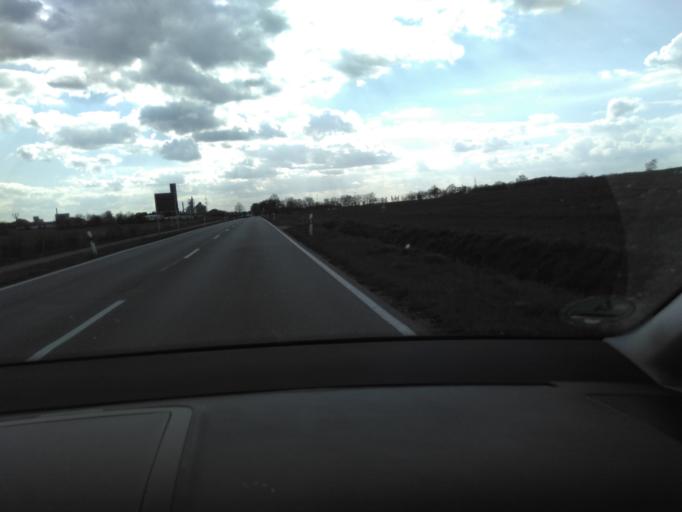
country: DE
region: North Rhine-Westphalia
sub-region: Regierungsbezirk Munster
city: Beckum
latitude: 51.7681
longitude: 8.0948
